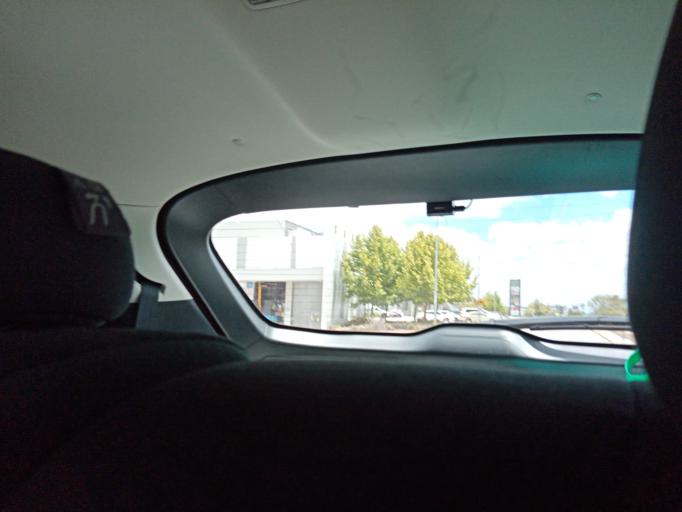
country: AU
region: Western Australia
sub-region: City of Cockburn
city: Success
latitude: -32.1308
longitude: 115.8587
